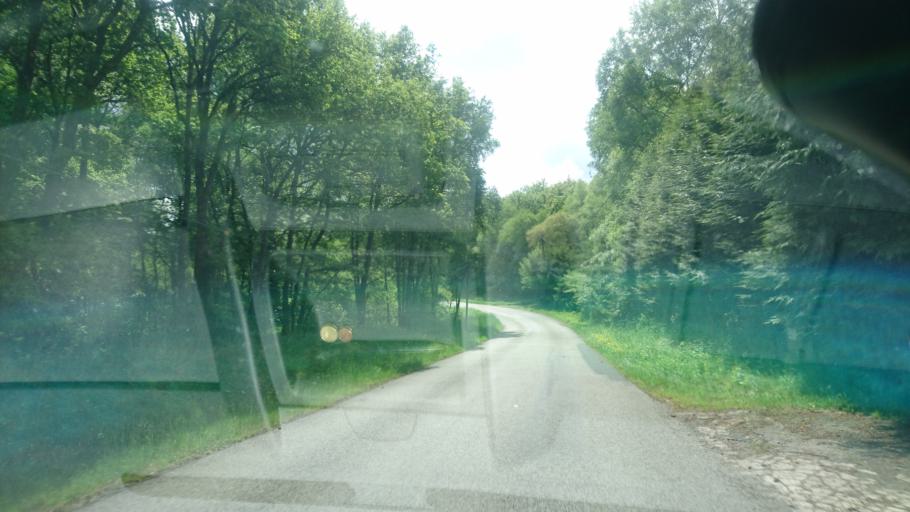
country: FR
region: Limousin
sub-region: Departement de la Haute-Vienne
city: Peyrat-le-Chateau
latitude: 45.7884
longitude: 1.8886
